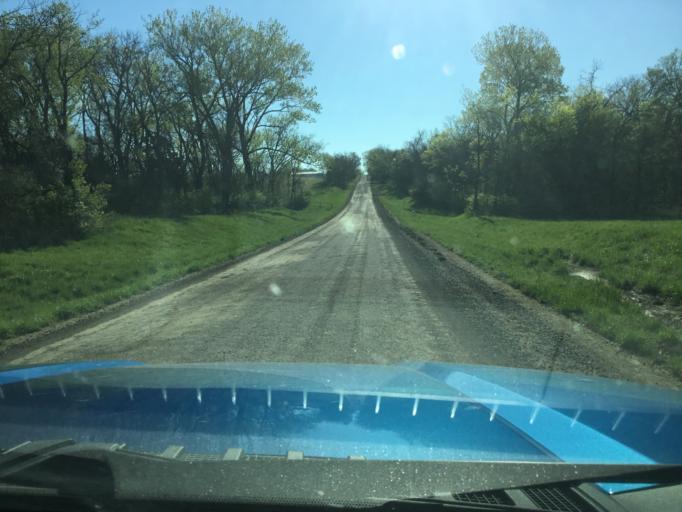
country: US
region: Kansas
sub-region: Douglas County
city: Lawrence
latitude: 38.9569
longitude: -95.3638
